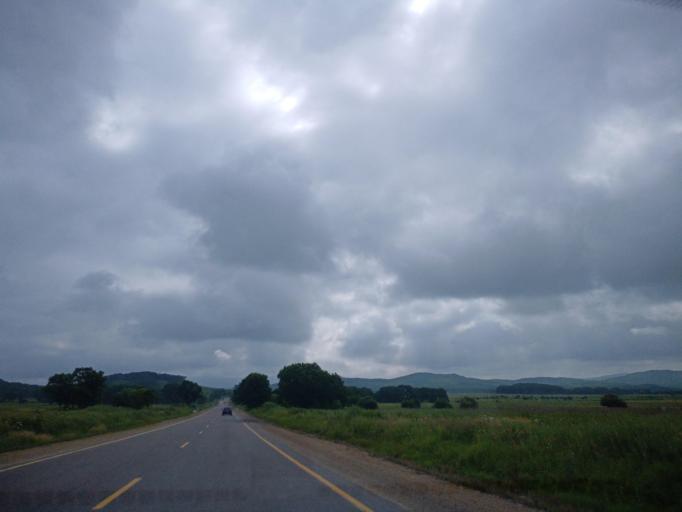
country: RU
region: Primorskiy
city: Dal'nerechensk
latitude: 46.0380
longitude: 133.8723
